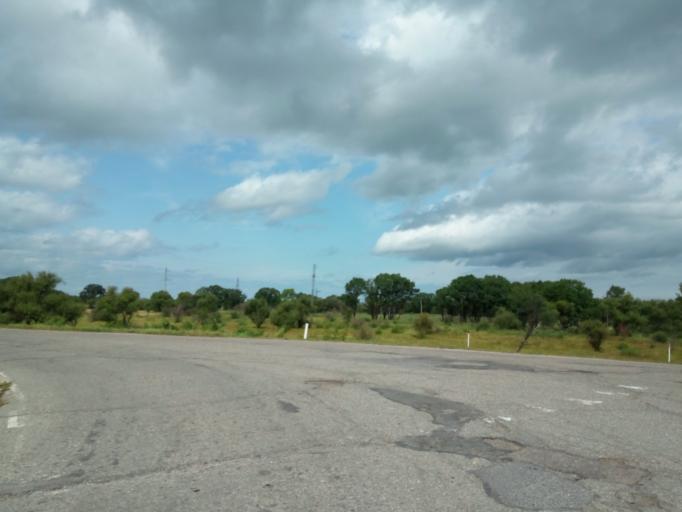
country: RU
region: Primorskiy
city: Dal'nerechensk
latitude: 45.9708
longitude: 133.7862
